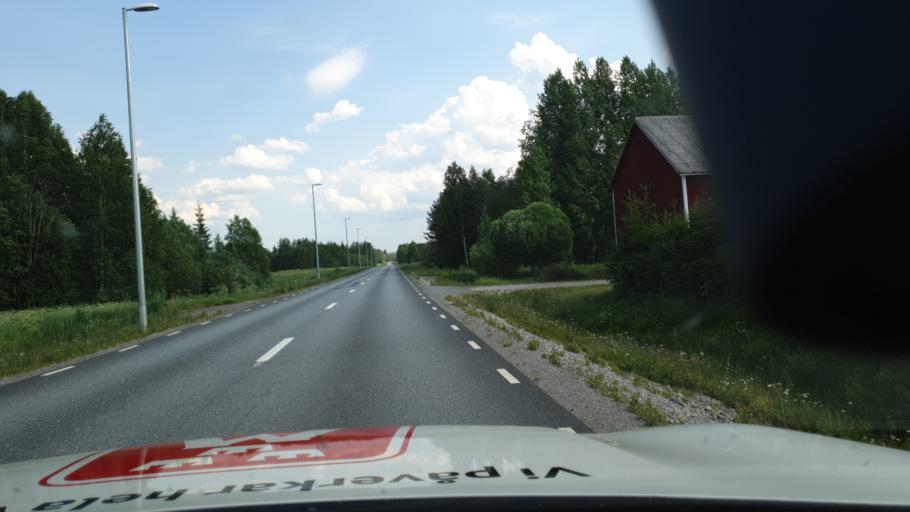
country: SE
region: Vaesterbotten
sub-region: Skelleftea Kommun
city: Forsbacka
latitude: 64.6987
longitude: 20.4733
